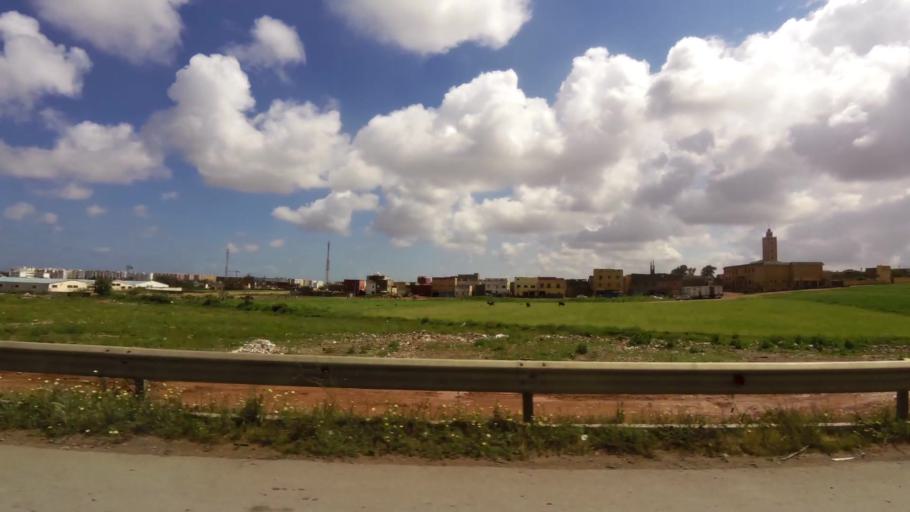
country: MA
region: Grand Casablanca
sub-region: Nouaceur
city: Dar Bouazza
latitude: 33.5387
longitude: -7.7125
